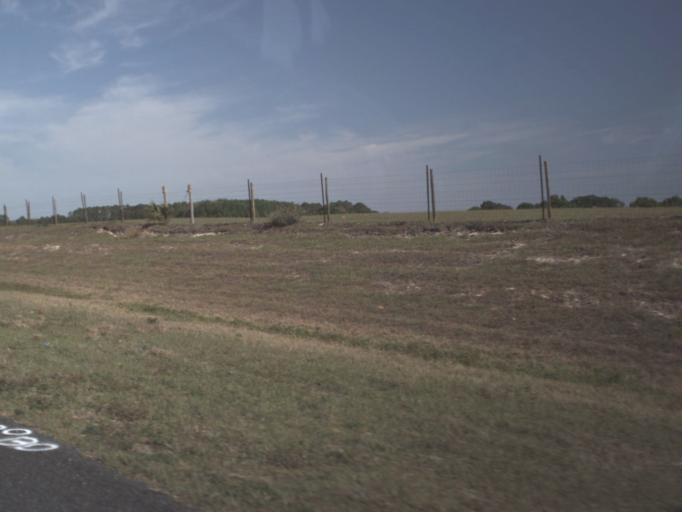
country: US
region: Florida
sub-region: Lake County
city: Mascotte
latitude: 28.6489
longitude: -81.8326
